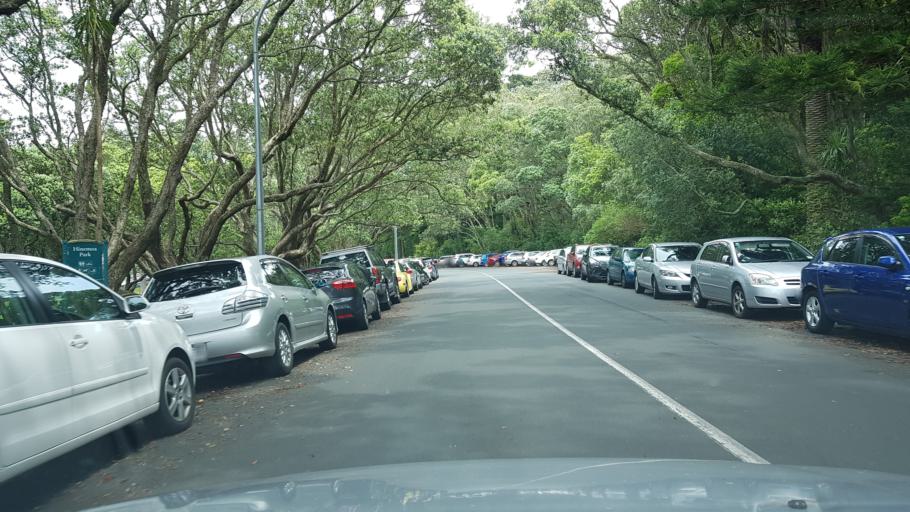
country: NZ
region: Auckland
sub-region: Auckland
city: North Shore
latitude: -36.8213
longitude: 174.7356
